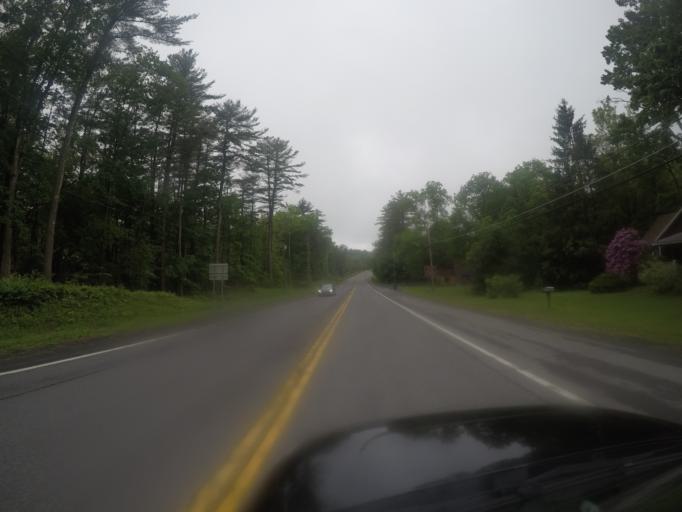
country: US
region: New York
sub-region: Ulster County
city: West Hurley
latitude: 41.9975
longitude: -74.1068
